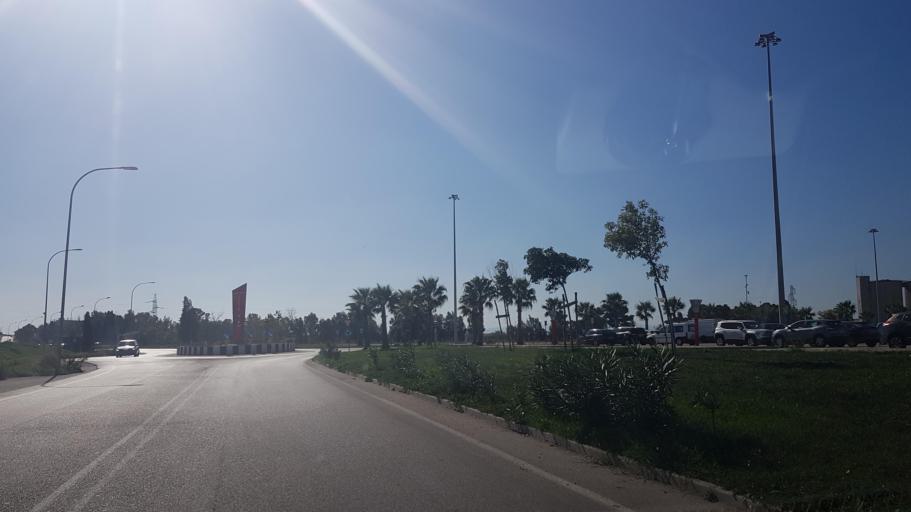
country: IT
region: Apulia
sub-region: Provincia di Foggia
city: Carapelle
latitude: 41.4145
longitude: 15.6540
